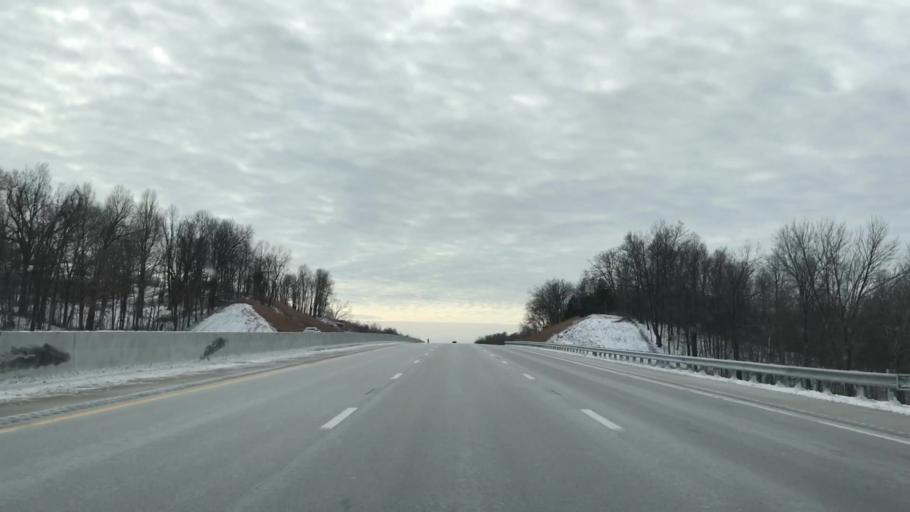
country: US
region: Kentucky
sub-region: Hart County
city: Munfordville
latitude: 37.3572
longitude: -85.8976
